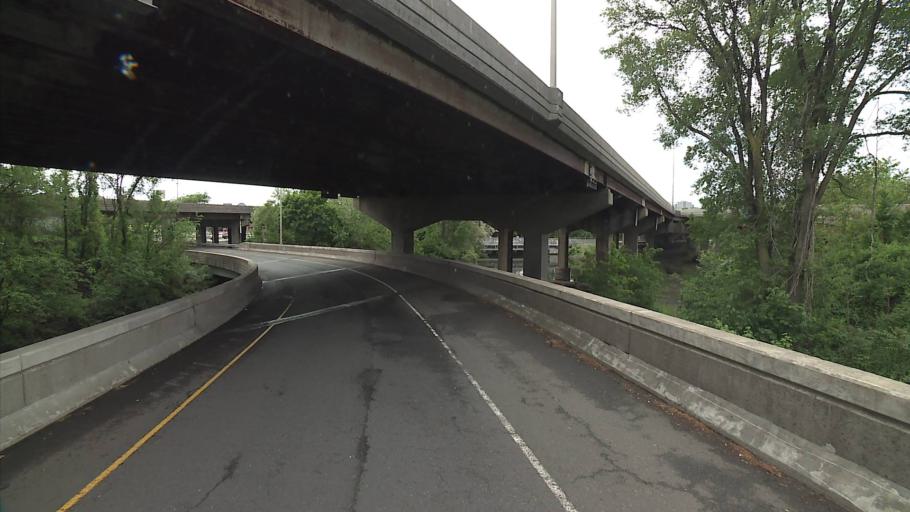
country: US
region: Connecticut
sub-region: New Haven County
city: New Haven
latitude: 41.3176
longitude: -72.9047
